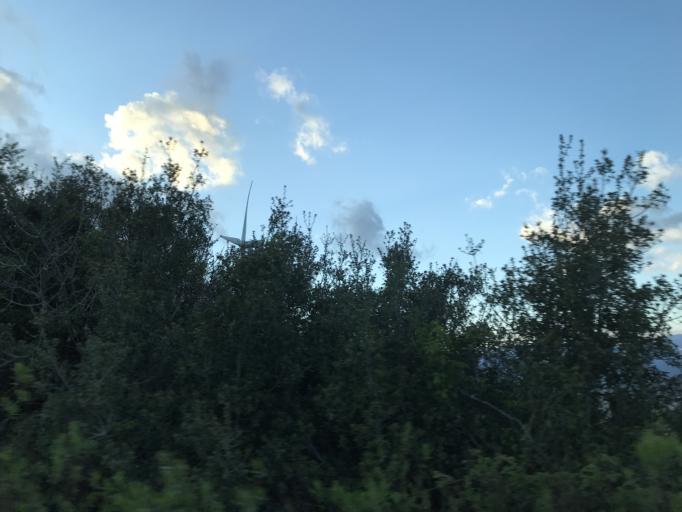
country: TR
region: Hatay
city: Buyukcat
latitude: 36.0944
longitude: 36.0368
